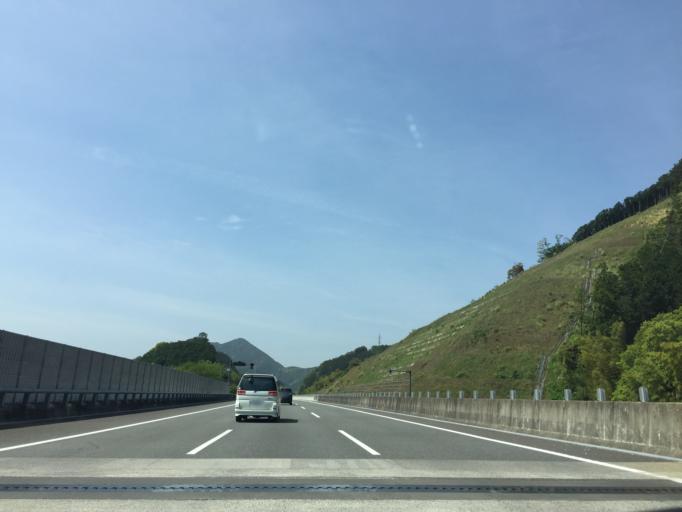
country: JP
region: Shizuoka
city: Shizuoka-shi
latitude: 35.0336
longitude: 138.3631
